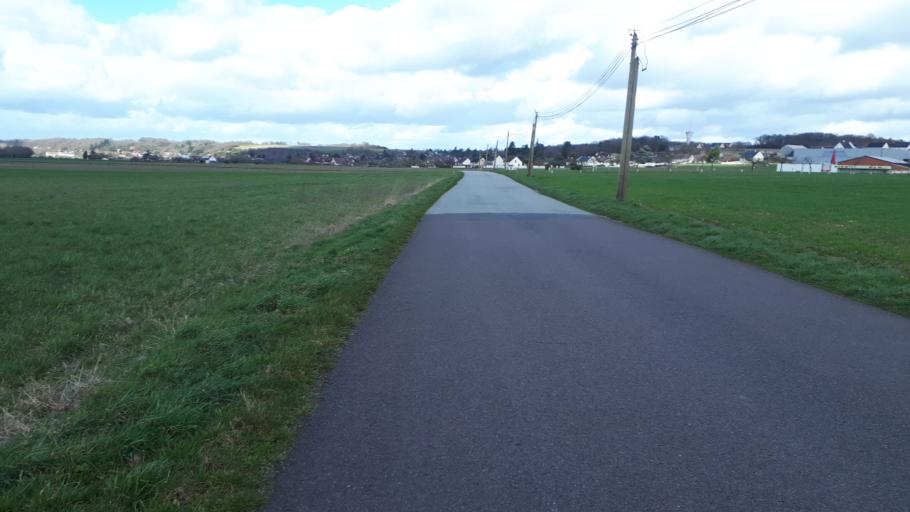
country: FR
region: Centre
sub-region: Departement du Loir-et-Cher
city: Villiers-sur-Loir
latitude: 47.7967
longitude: 1.0000
